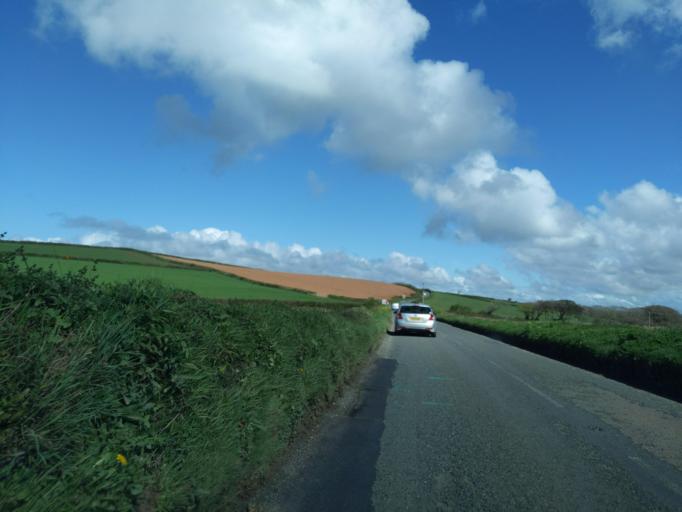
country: GB
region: England
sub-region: Cornwall
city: Wadebridge
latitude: 50.5753
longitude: -4.8147
